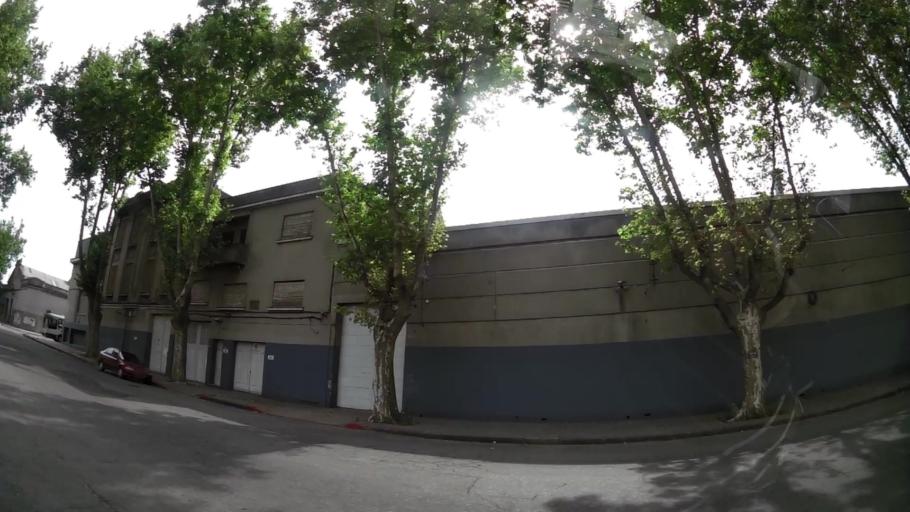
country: UY
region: Montevideo
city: Montevideo
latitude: -34.8874
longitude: -56.1944
